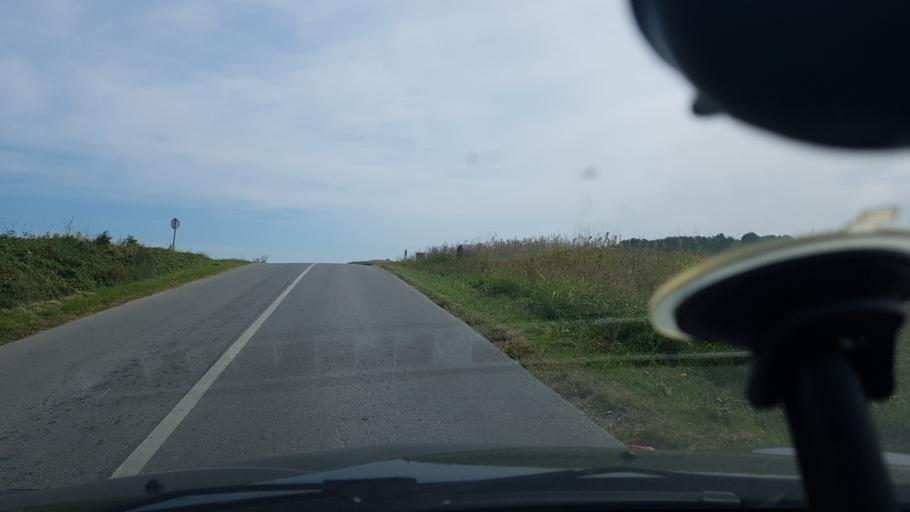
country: HR
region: Varazdinska
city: Ljubescica
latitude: 46.1016
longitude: 16.3530
